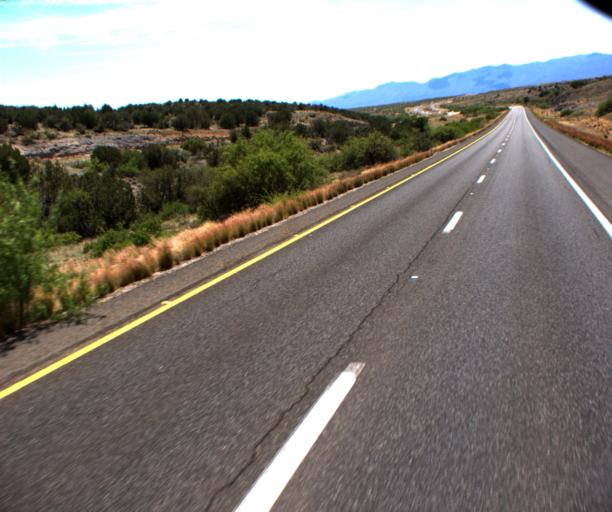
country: US
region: Arizona
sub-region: Yavapai County
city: Cornville
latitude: 34.7880
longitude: -111.9207
